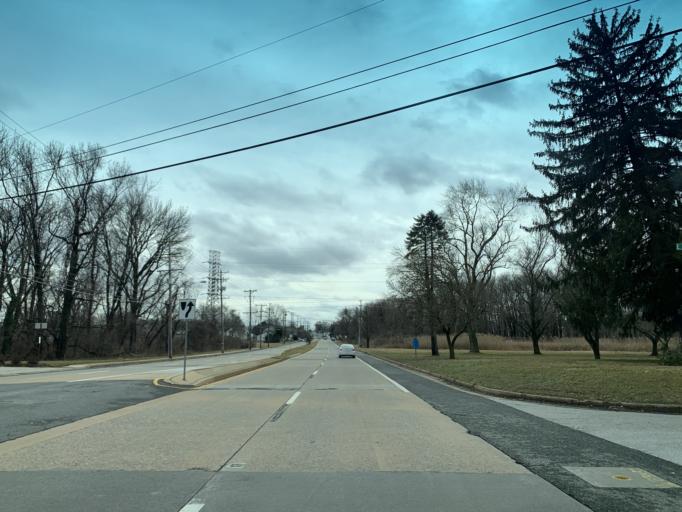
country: US
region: Delaware
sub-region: New Castle County
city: New Castle
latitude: 39.6785
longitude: -75.5599
